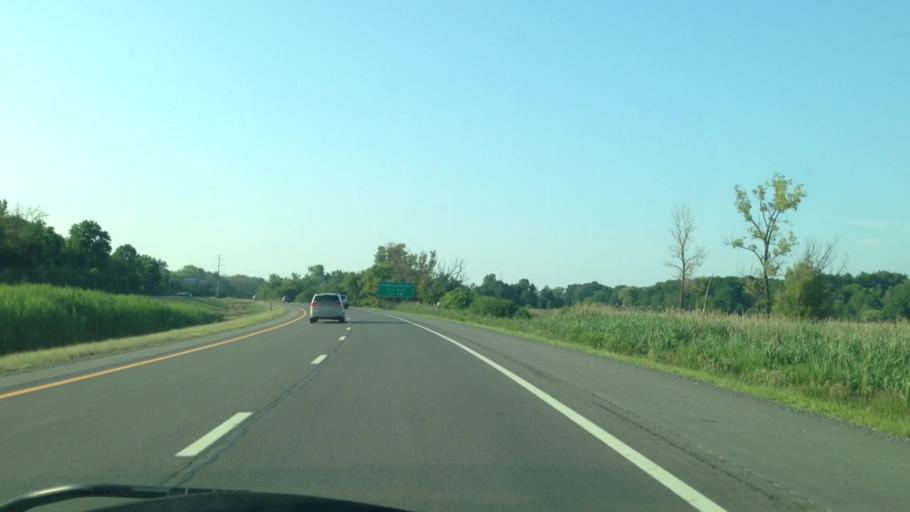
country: US
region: New York
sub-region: Onondaga County
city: East Syracuse
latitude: 43.0223
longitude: -76.0620
